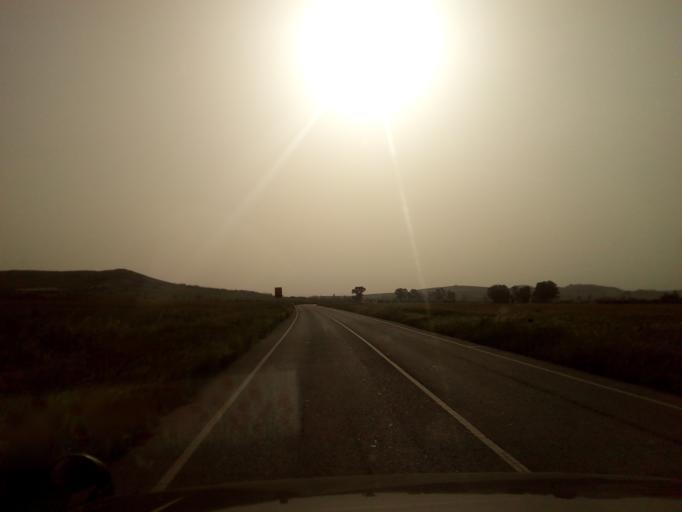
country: CY
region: Larnaka
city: Athienou
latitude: 35.0537
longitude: 33.5096
